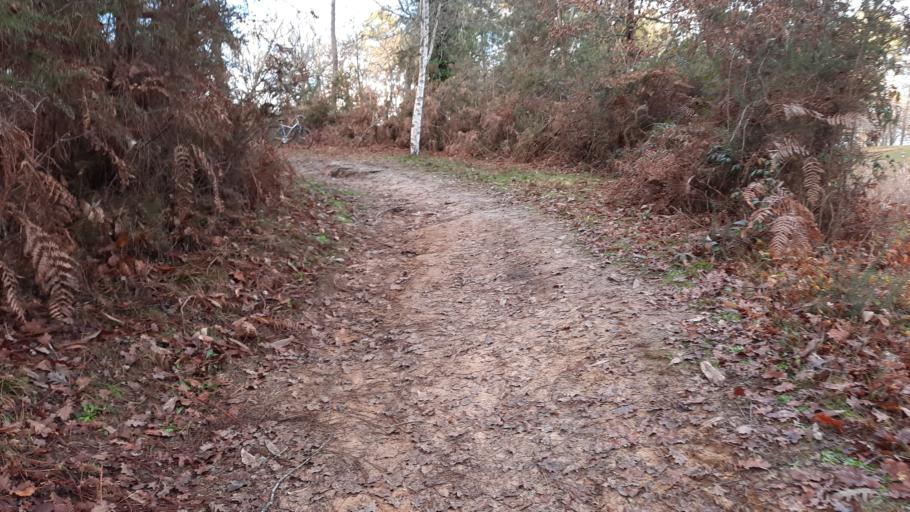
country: FR
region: Aquitaine
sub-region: Departement des Landes
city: Saint-Pierre-du-Mont
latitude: 43.8792
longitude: -0.5375
